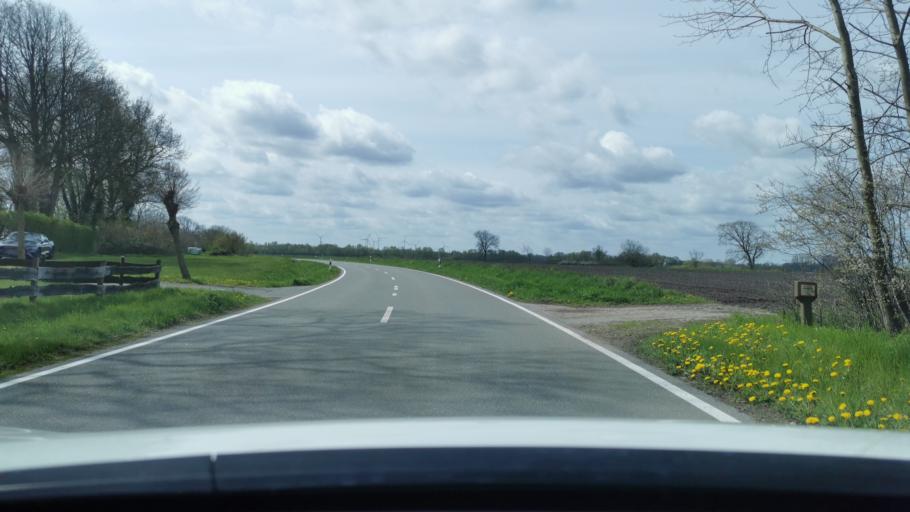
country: DE
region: Schleswig-Holstein
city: Oldenbuttel
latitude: 54.1912
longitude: 9.4528
